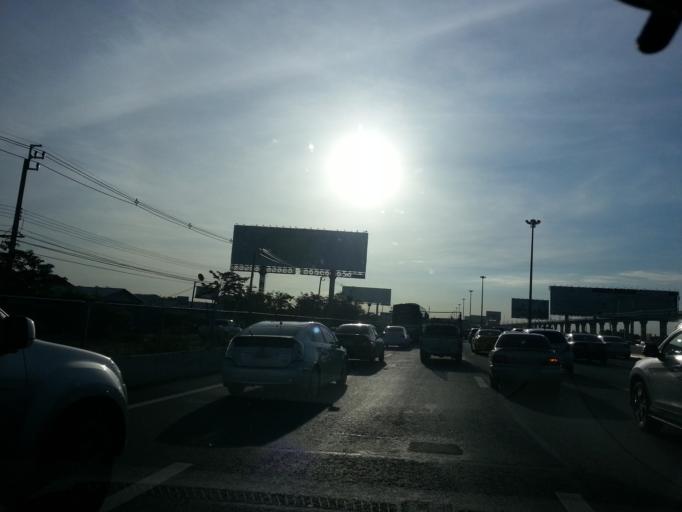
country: TH
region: Bangkok
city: Saphan Sung
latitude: 13.7317
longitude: 100.7126
